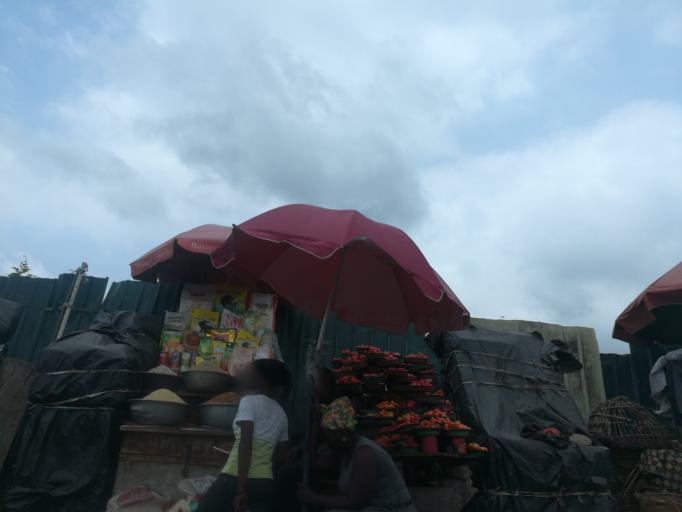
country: NG
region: Lagos
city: Lagos
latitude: 6.4519
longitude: 3.4021
